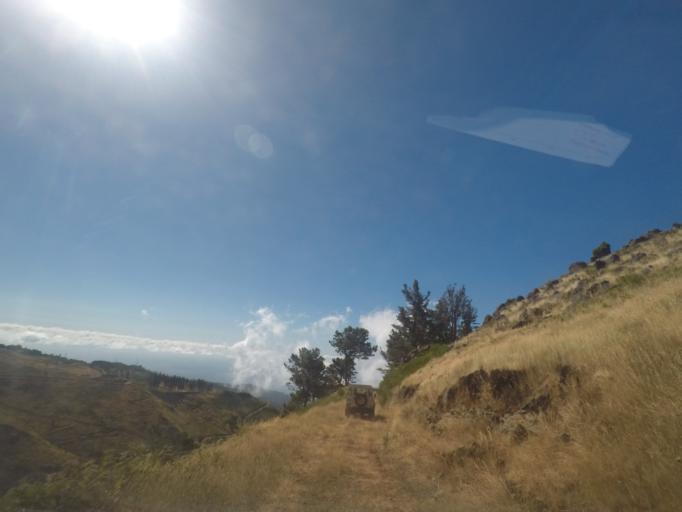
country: PT
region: Madeira
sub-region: Funchal
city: Nossa Senhora do Monte
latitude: 32.7074
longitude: -16.9067
